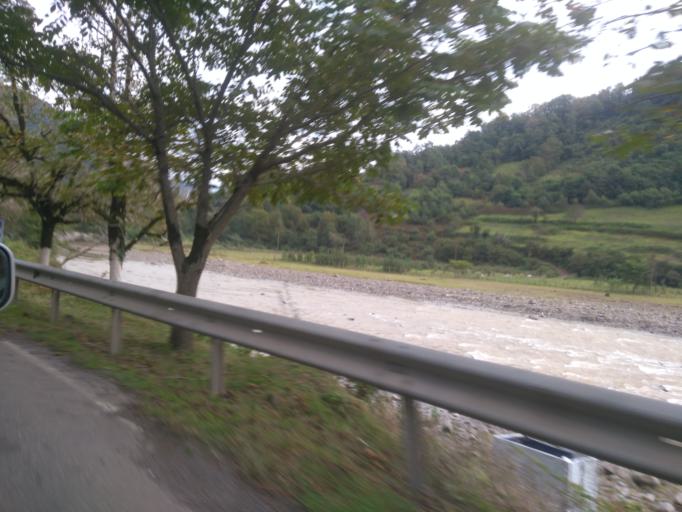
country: TR
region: Artvin
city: Camili
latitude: 41.5623
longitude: 41.8242
